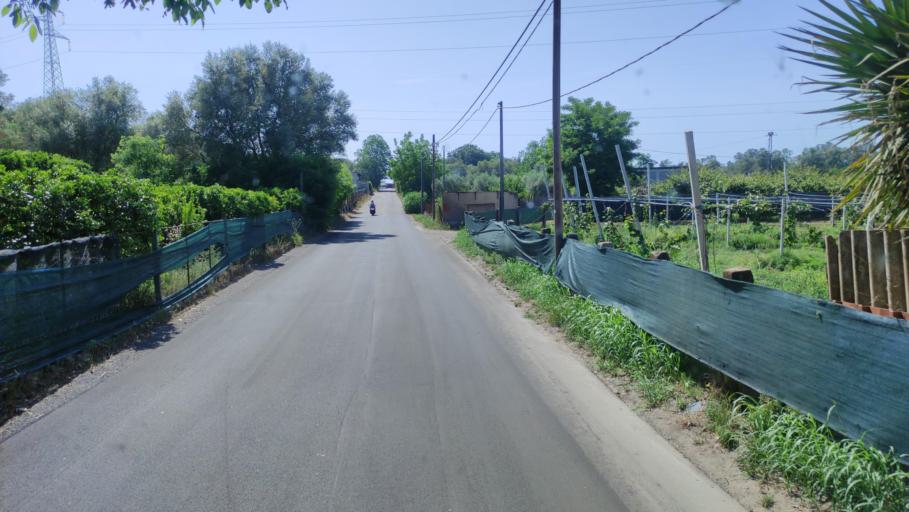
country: IT
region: Calabria
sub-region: Provincia di Reggio Calabria
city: Rosarno
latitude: 38.4548
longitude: 15.9780
